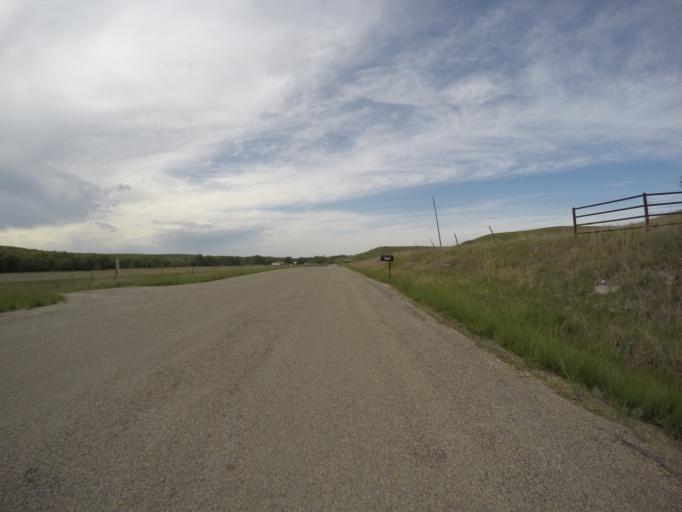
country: US
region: Kansas
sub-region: Riley County
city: Ogden
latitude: 38.9826
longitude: -96.5897
